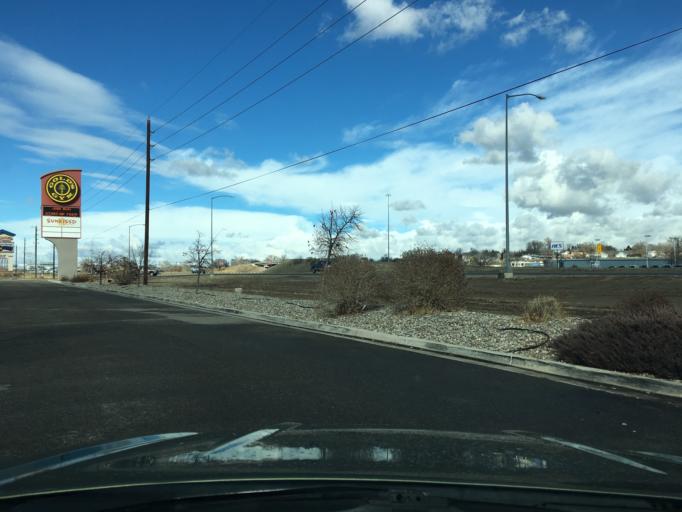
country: US
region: Colorado
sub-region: Mesa County
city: Grand Junction
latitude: 39.0748
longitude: -108.5757
